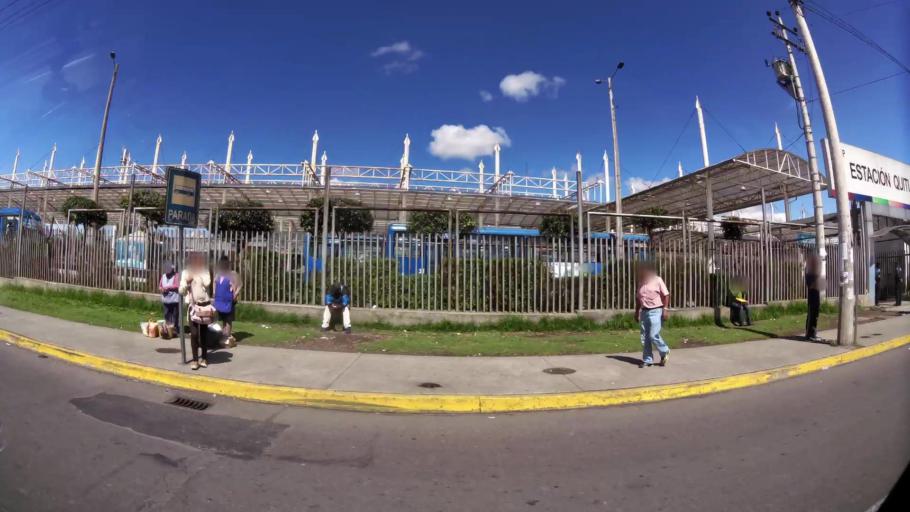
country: EC
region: Pichincha
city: Quito
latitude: -0.2955
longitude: -78.5551
